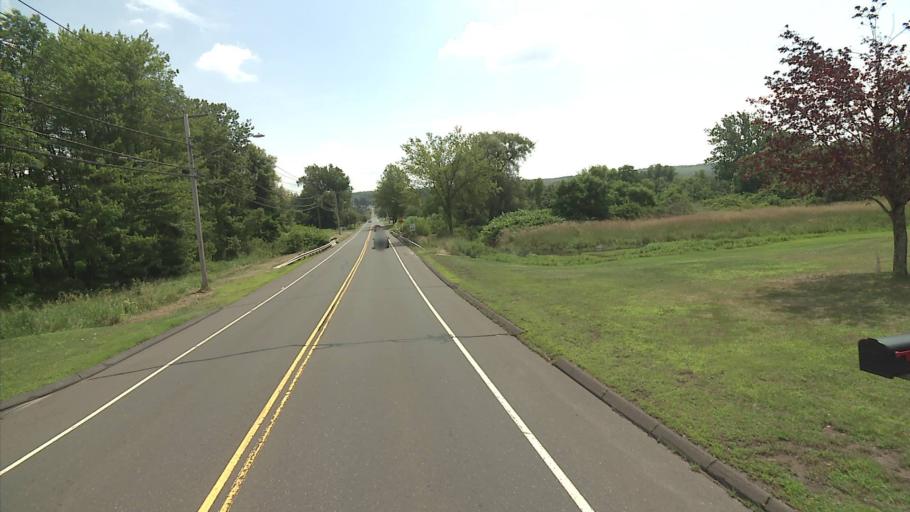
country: US
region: Connecticut
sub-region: Middlesex County
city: Middletown
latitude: 41.5335
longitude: -72.6331
